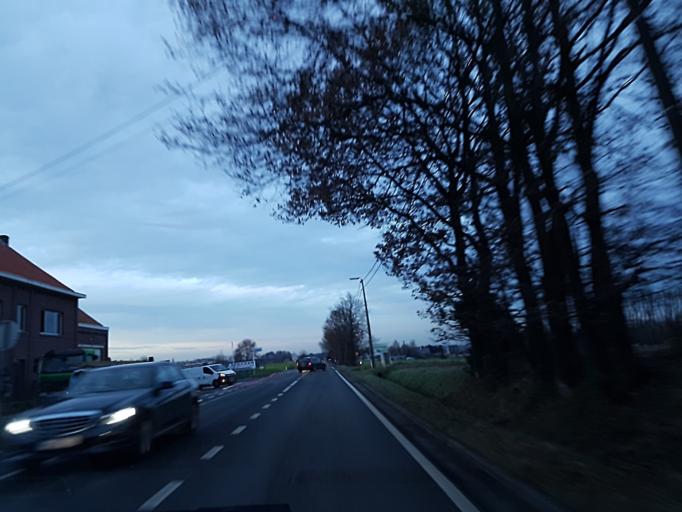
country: BE
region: Flanders
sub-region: Provincie Vlaams-Brabant
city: Lubbeek
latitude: 50.8771
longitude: 4.8811
